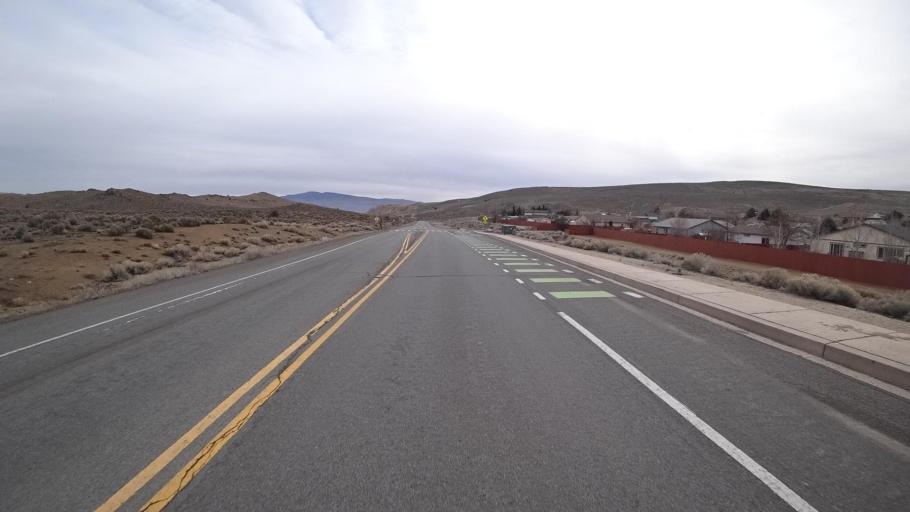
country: US
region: Nevada
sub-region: Washoe County
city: Sun Valley
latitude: 39.6073
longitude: -119.7562
